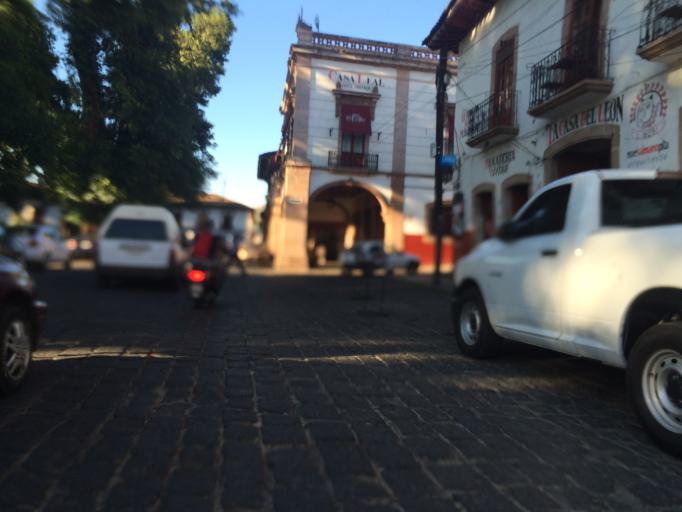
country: MX
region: Michoacan
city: Patzcuaro
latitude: 19.5130
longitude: -101.6085
